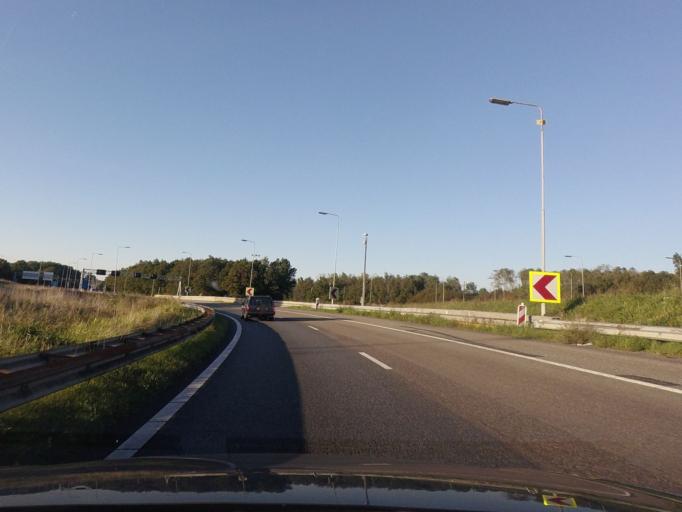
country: NL
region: North Holland
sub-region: Gemeente Velsen
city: Velsen-Zuid
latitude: 52.4526
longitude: 4.6586
